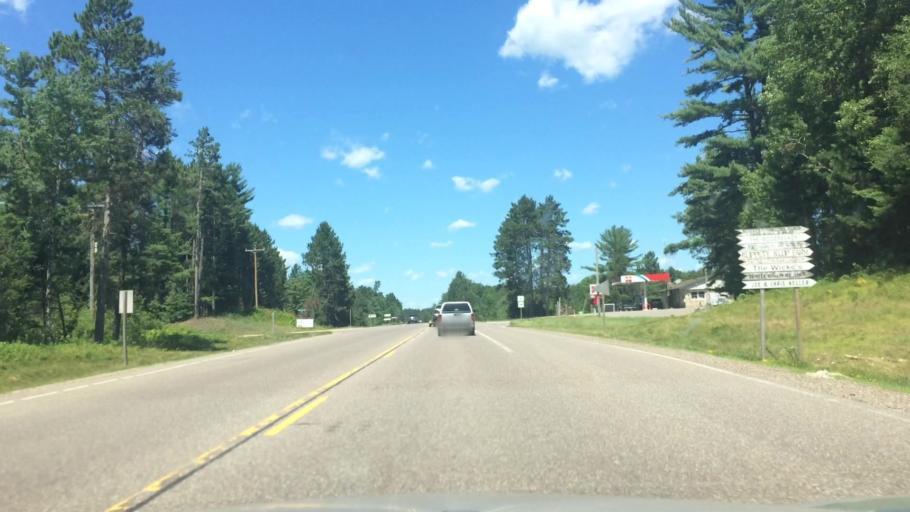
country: US
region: Wisconsin
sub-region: Lincoln County
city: Tomahawk
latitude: 45.6439
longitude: -89.7050
